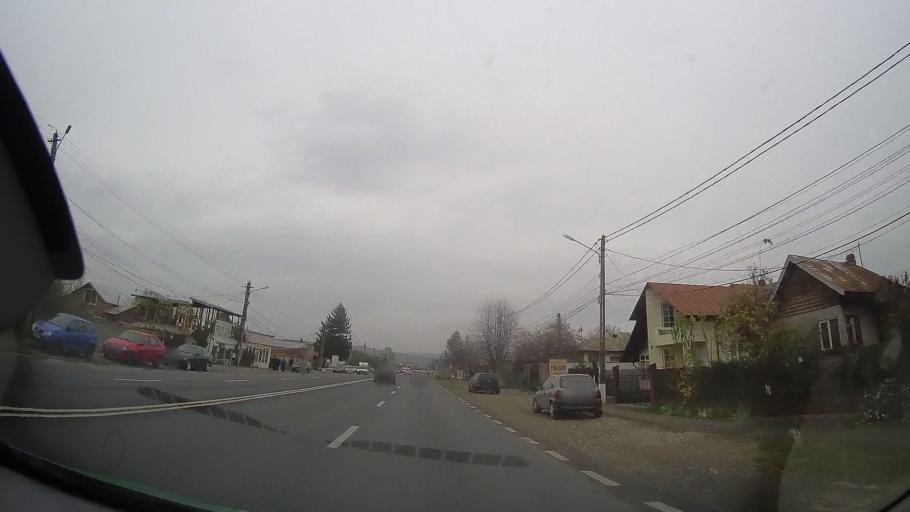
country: RO
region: Prahova
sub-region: Comuna Bucov
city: Bucov
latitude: 44.9728
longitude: 26.0794
